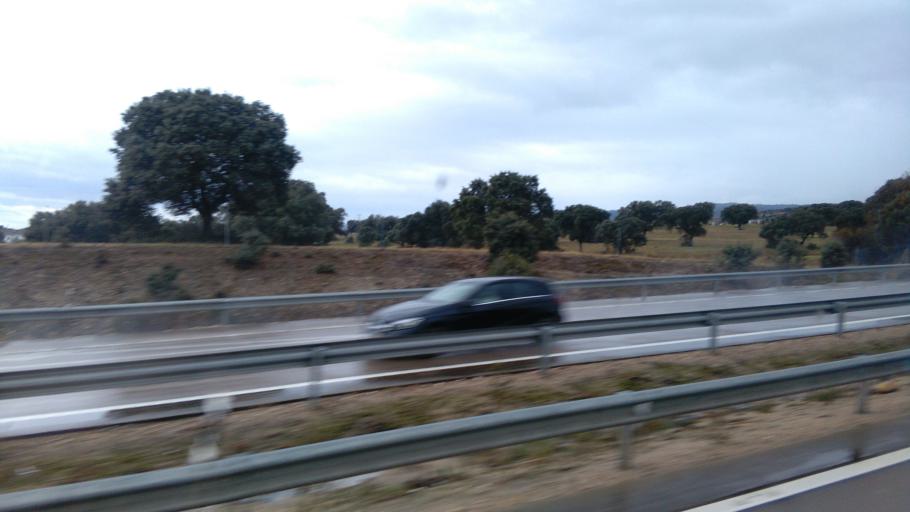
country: ES
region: Castille-La Mancha
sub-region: Province of Toledo
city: Cervera de los Montes
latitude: 40.0147
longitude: -4.7827
